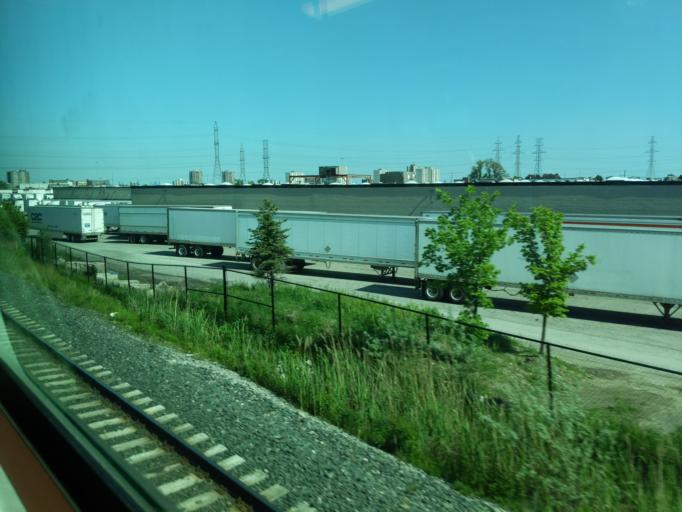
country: CA
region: Ontario
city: Etobicoke
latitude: 43.7062
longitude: -79.5702
